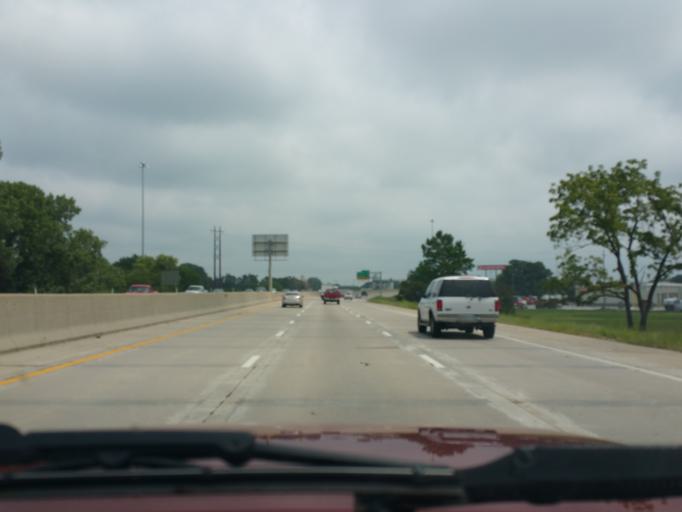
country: US
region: Kansas
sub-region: Shawnee County
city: Topeka
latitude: 39.0692
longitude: -95.7128
